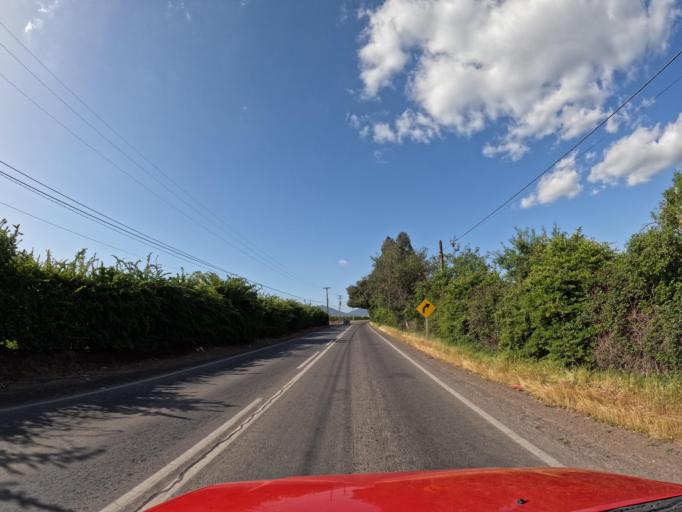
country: CL
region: Maule
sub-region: Provincia de Curico
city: Rauco
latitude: -34.9030
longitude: -71.2768
